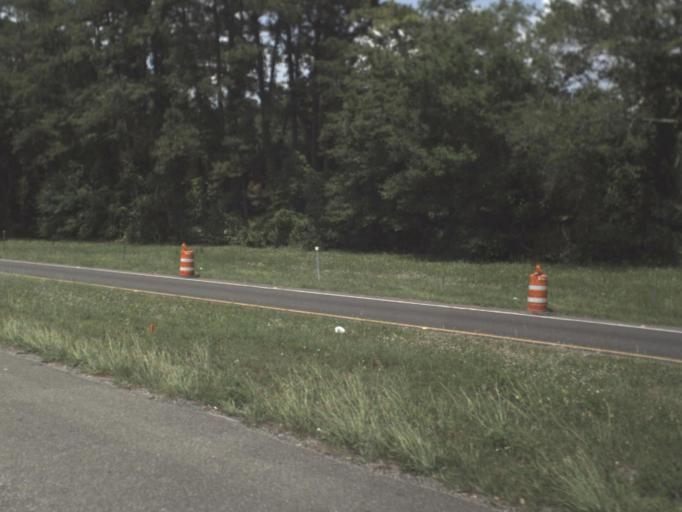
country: US
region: Florida
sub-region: Clay County
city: Bellair-Meadowbrook Terrace
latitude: 30.2724
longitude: -81.7681
